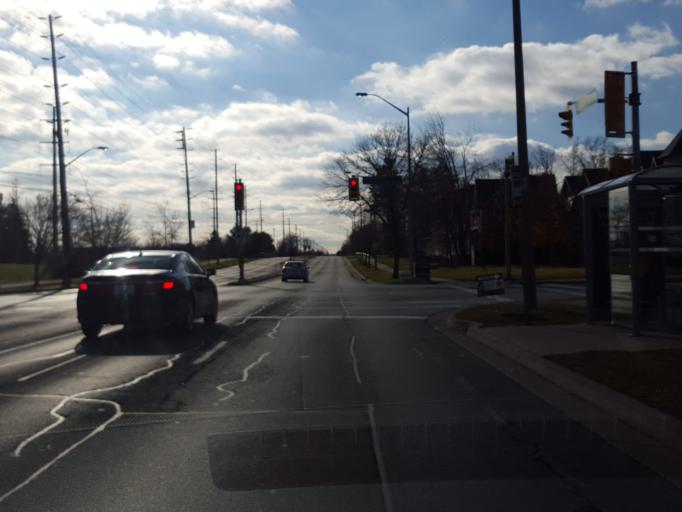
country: CA
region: Ontario
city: Burlington
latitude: 43.3838
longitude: -79.8013
